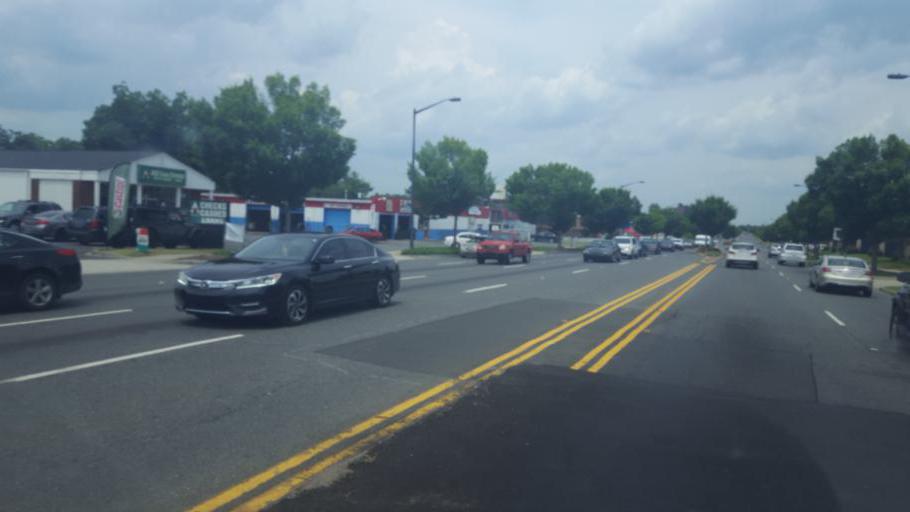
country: US
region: South Carolina
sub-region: York County
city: Rock Hill
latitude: 34.9633
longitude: -81.0012
